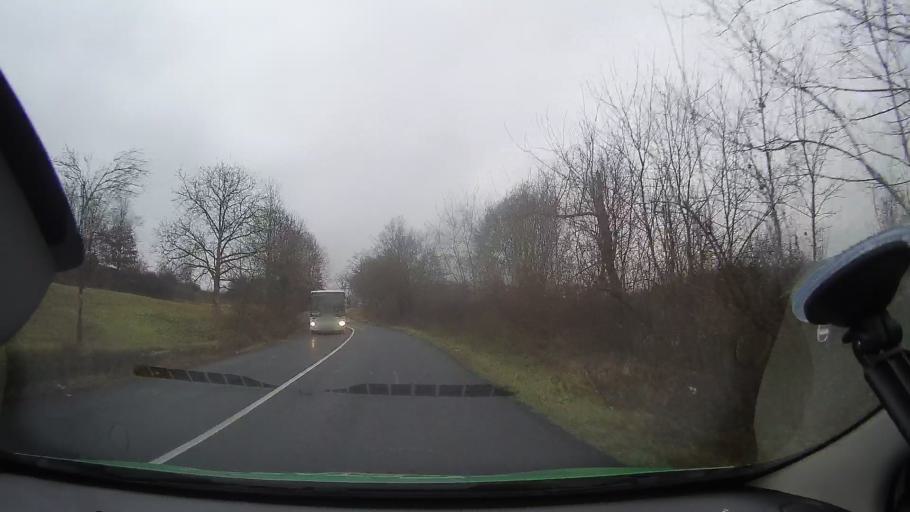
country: RO
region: Arad
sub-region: Comuna Varfurile
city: Varfurile
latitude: 46.3261
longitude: 22.4932
